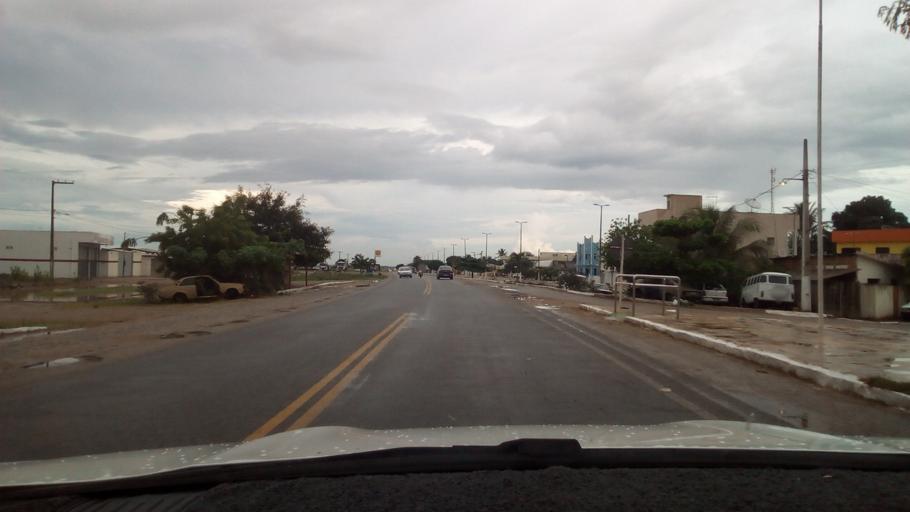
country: BR
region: Paraiba
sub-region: Mari
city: Mari
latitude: -7.0544
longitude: -35.3169
